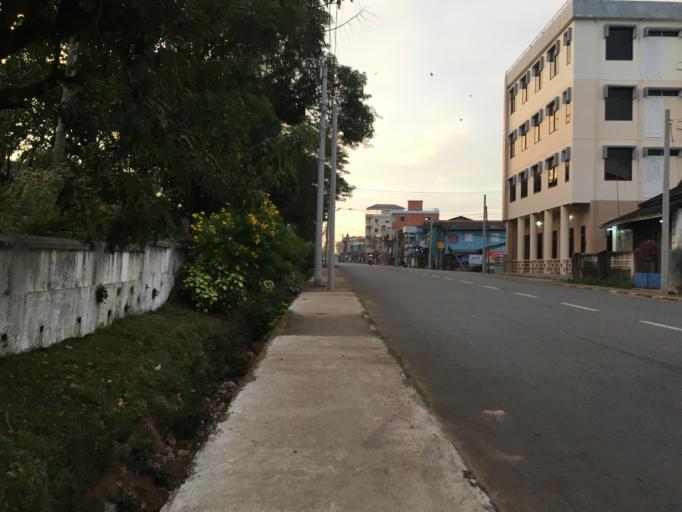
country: MM
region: Mon
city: Mawlamyine
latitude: 16.4715
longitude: 97.6254
